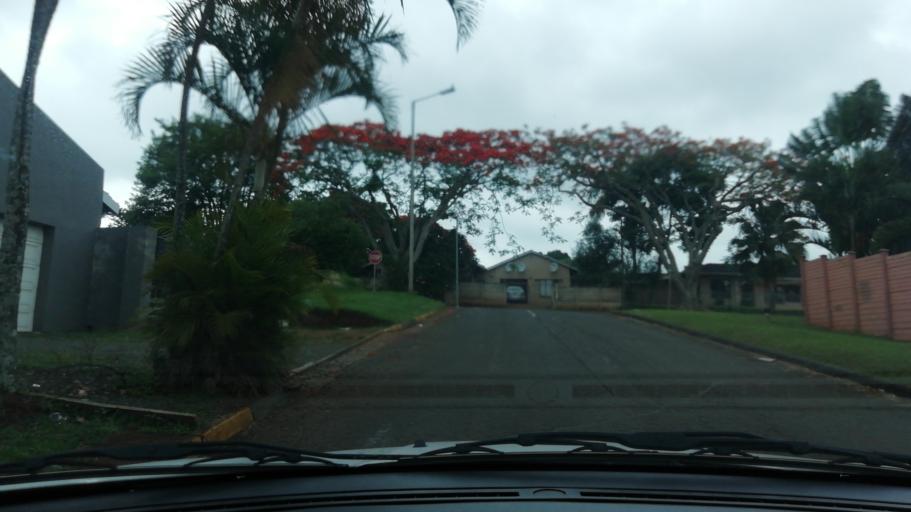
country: ZA
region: KwaZulu-Natal
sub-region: uThungulu District Municipality
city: Empangeni
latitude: -28.7649
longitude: 31.8996
